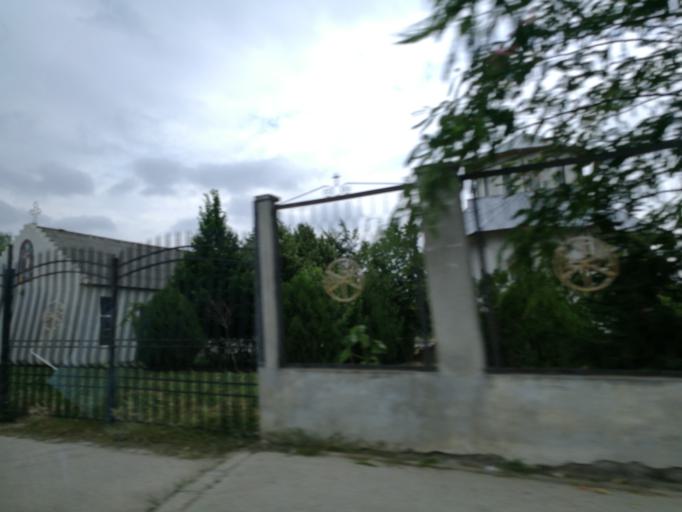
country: RO
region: Constanta
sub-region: Municipiul Mangalia
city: Mangalia
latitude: 43.8164
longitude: 28.5734
